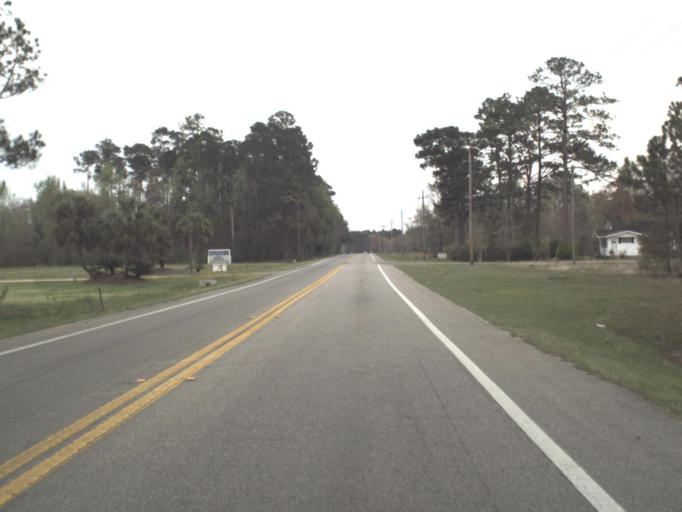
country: US
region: Florida
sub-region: Gulf County
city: Wewahitchka
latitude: 30.1365
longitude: -85.2089
